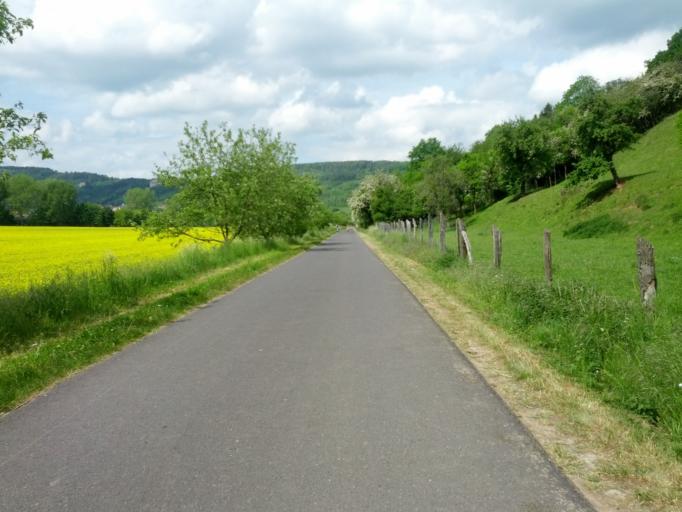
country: DE
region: Thuringia
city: Treffurt
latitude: 51.1219
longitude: 10.2521
